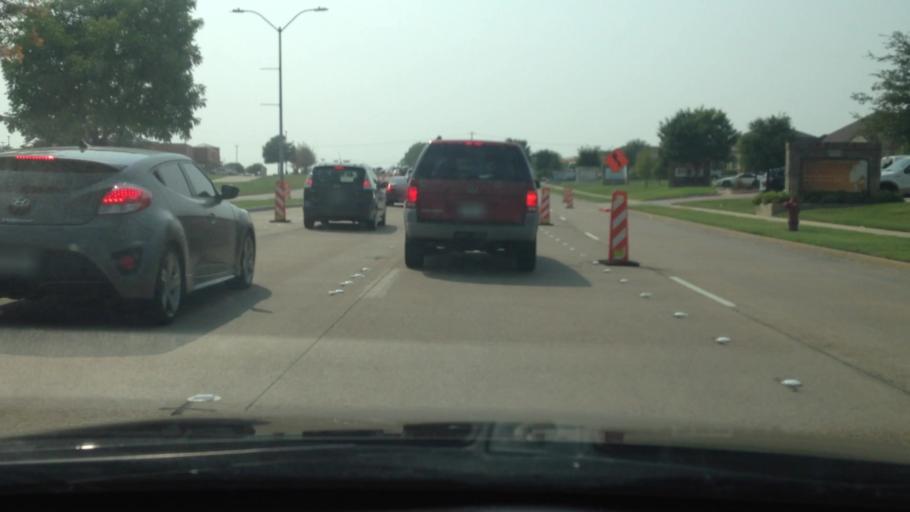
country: US
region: Texas
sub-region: Tarrant County
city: North Richland Hills
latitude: 32.8619
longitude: -97.2057
